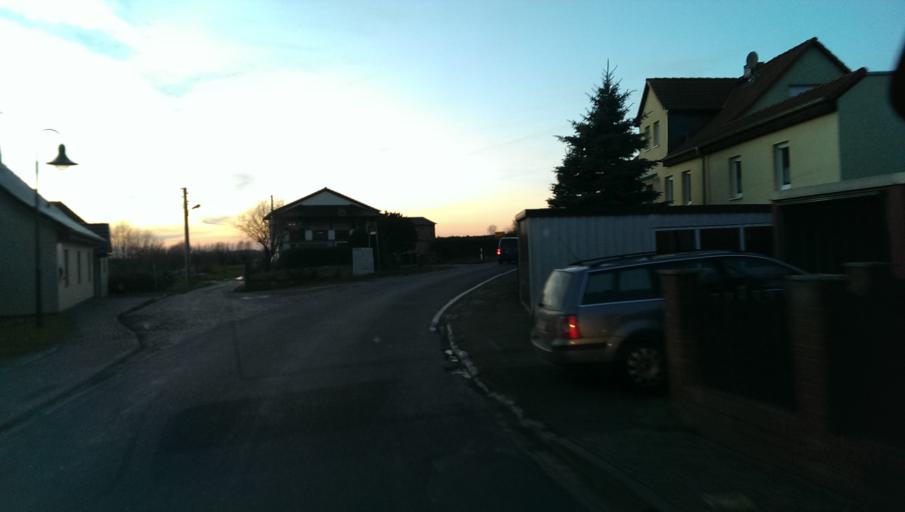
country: DE
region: Saxony-Anhalt
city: Ausleben
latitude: 52.0925
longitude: 11.1508
